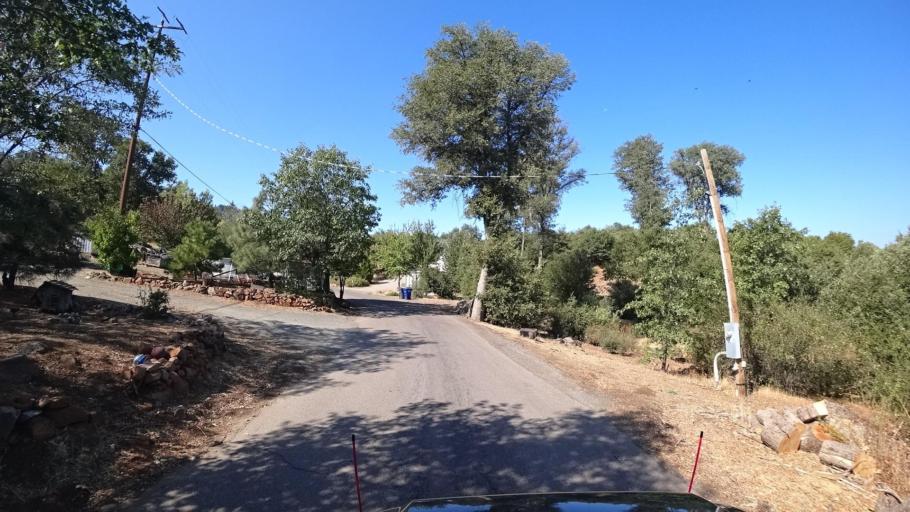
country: US
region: California
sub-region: San Diego County
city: Julian
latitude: 33.0233
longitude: -116.5776
